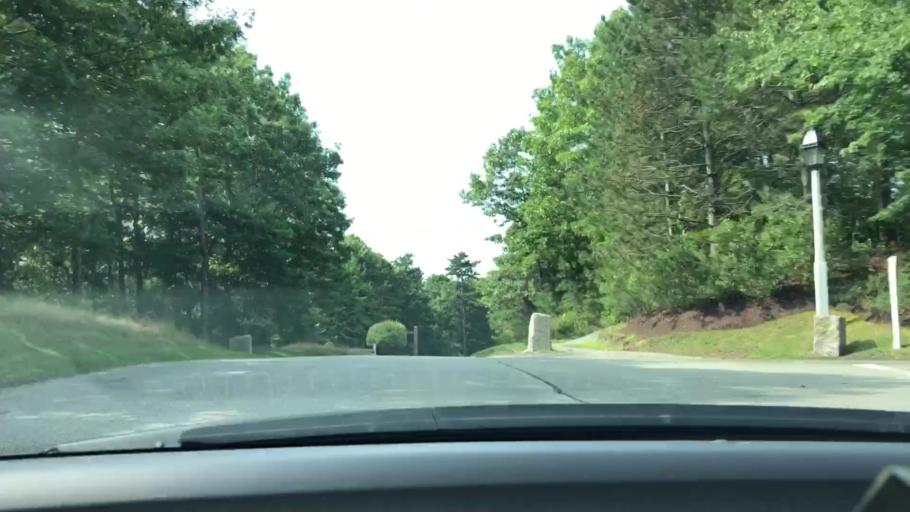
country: US
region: Massachusetts
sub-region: Plymouth County
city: Plymouth
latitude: 41.8907
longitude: -70.5997
